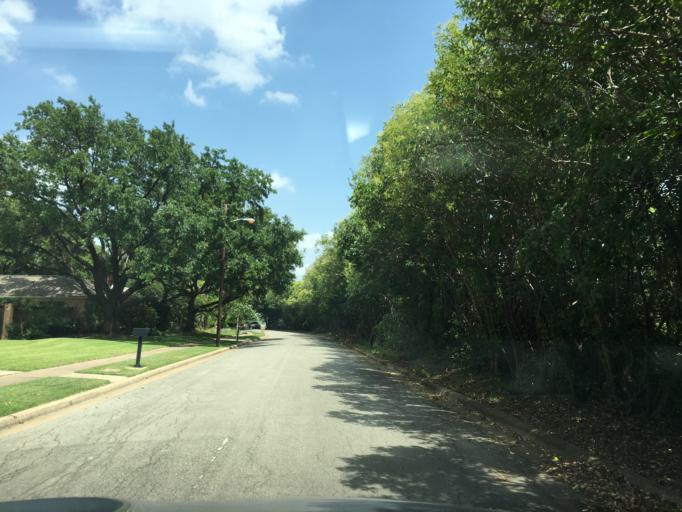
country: US
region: Texas
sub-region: Dallas County
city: University Park
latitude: 32.8966
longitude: -96.7819
